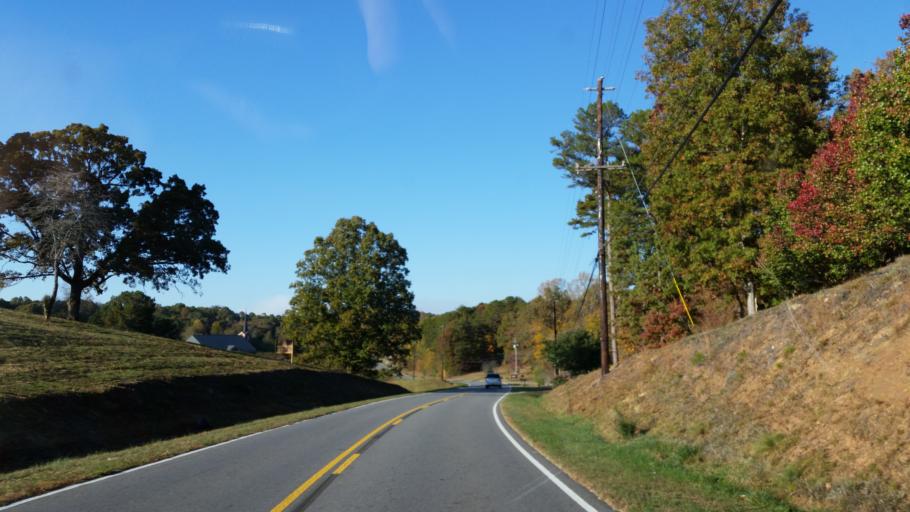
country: US
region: Georgia
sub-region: Gilmer County
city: Ellijay
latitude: 34.6644
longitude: -84.4731
